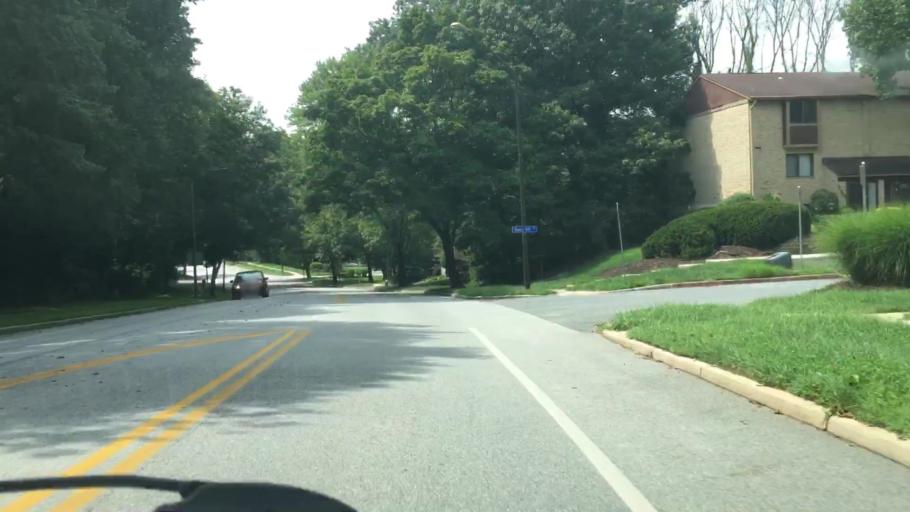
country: US
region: Maryland
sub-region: Howard County
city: Riverside
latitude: 39.1859
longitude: -76.8469
